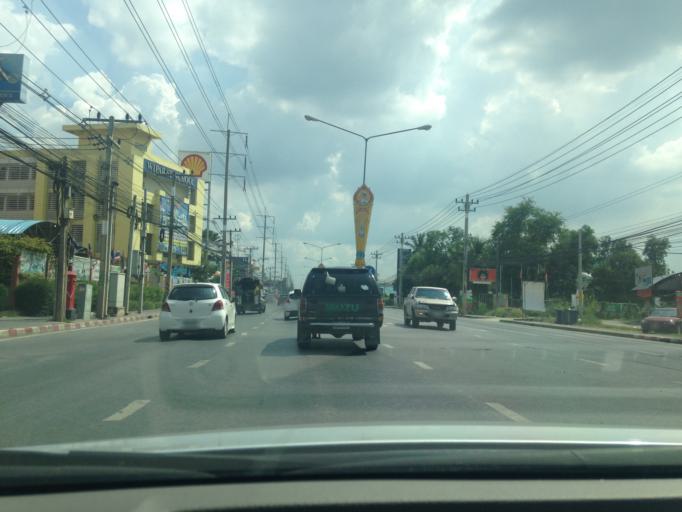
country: TH
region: Pathum Thani
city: Sam Khok
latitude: 14.0409
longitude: 100.5252
